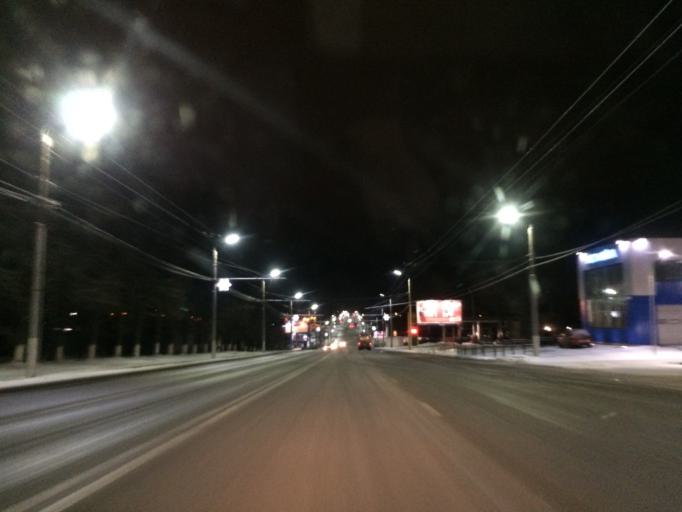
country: RU
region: Tula
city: Gorelki
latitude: 54.2422
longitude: 37.6178
